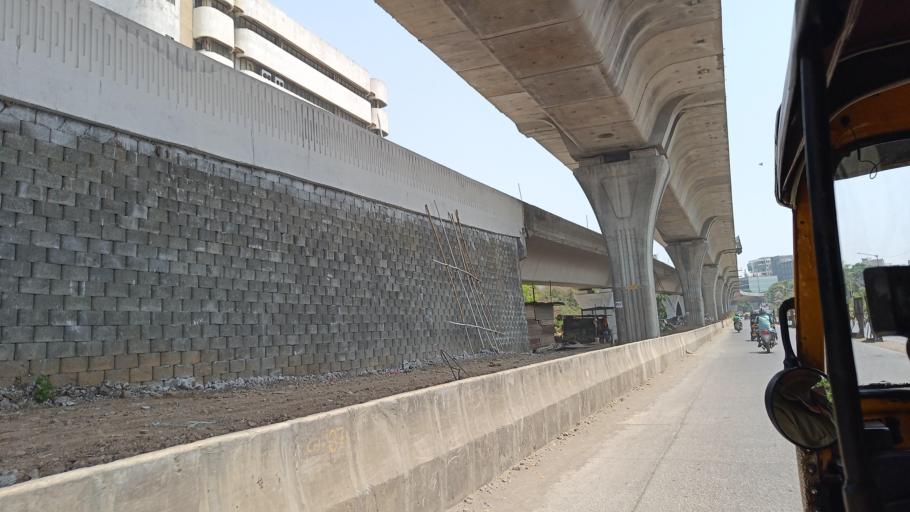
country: IN
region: Maharashtra
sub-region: Mumbai Suburban
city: Mumbai
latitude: 19.0757
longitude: 72.8572
